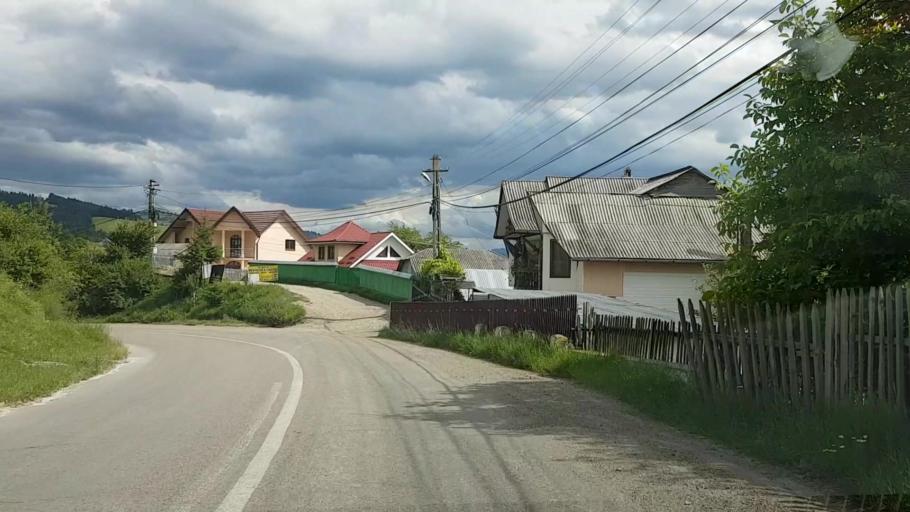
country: RO
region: Neamt
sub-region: Comuna Hangu
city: Hangu
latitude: 47.0238
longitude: 26.0695
